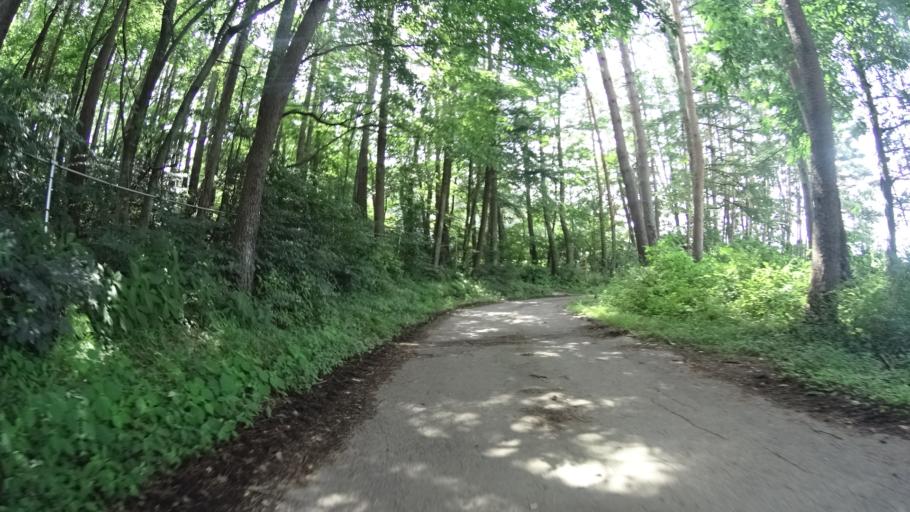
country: JP
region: Yamanashi
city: Nirasaki
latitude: 35.8966
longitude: 138.4732
